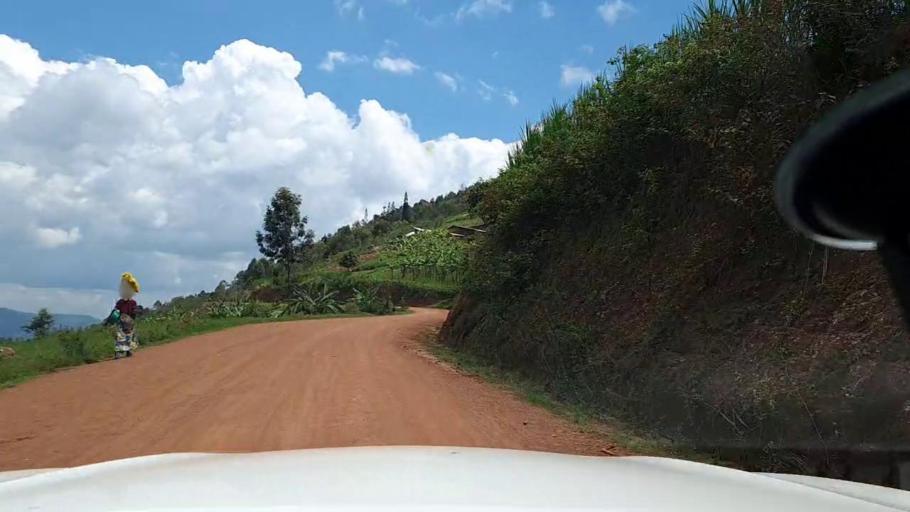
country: RW
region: Kigali
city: Kigali
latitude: -1.7826
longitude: 29.8408
